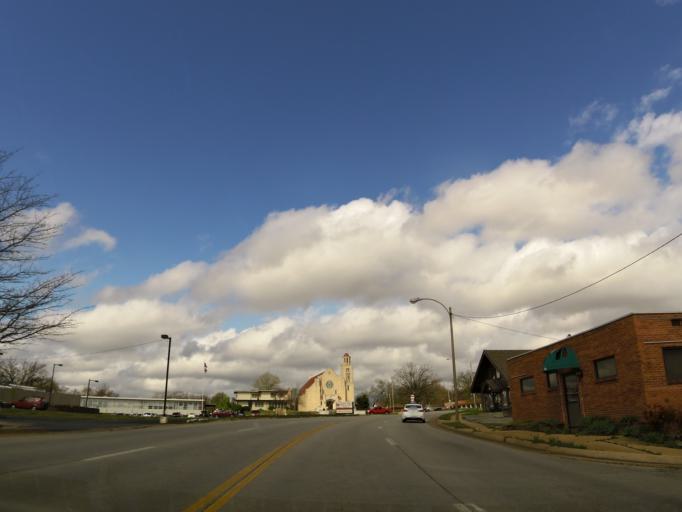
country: US
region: Missouri
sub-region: Butler County
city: Poplar Bluff
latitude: 36.7579
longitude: -90.3986
